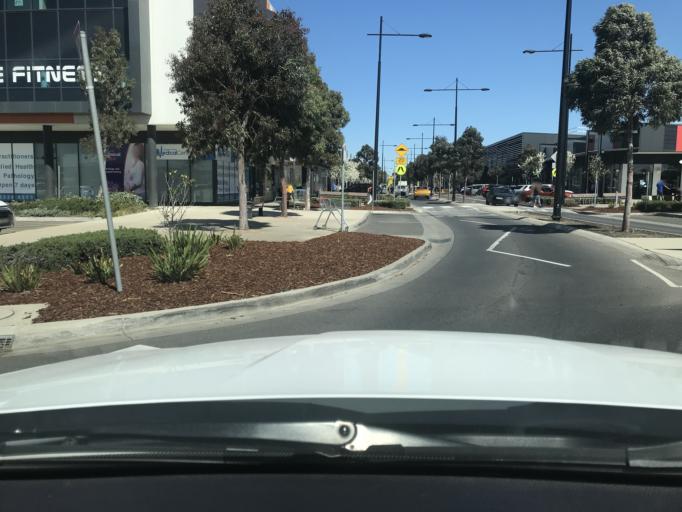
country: AU
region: Victoria
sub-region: Hume
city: Roxburgh Park
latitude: -37.5915
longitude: 144.9145
